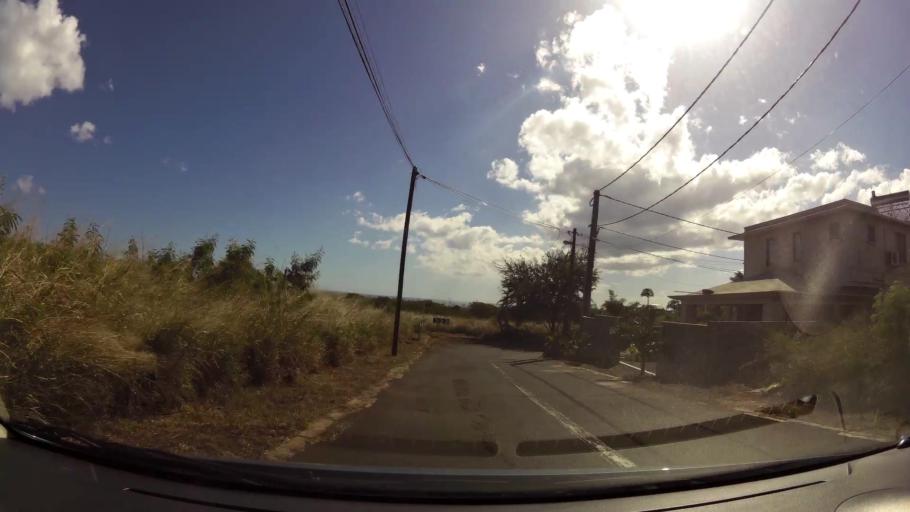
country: MU
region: Black River
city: Albion
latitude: -20.2254
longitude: 57.4134
